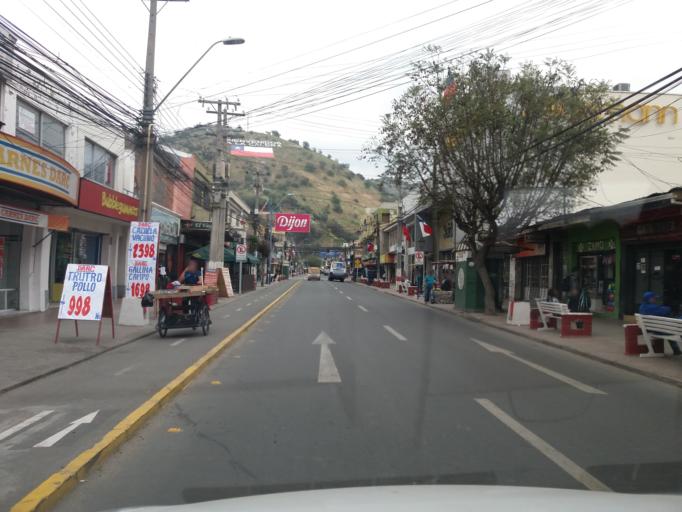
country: CL
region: Valparaiso
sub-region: Provincia de Quillota
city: Hacienda La Calera
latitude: -32.7873
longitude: -71.1897
